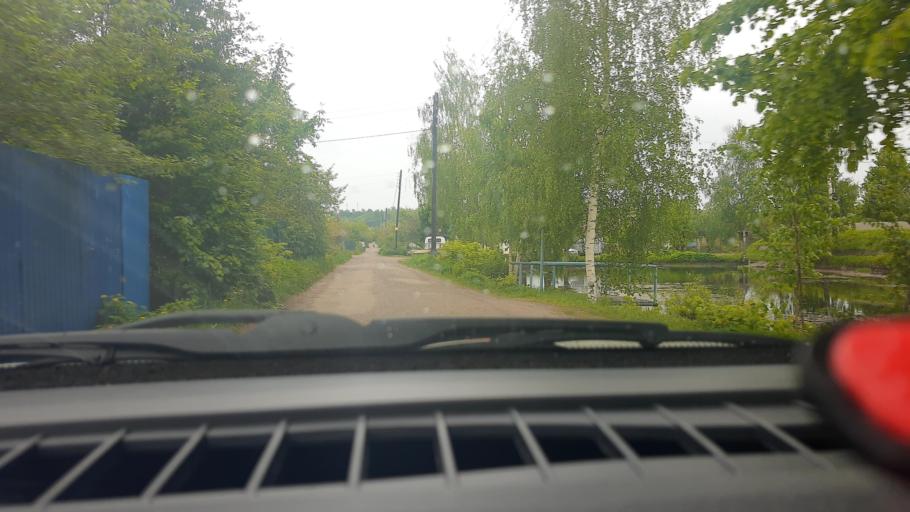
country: RU
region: Nizjnij Novgorod
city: Burevestnik
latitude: 56.2168
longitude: 43.8511
